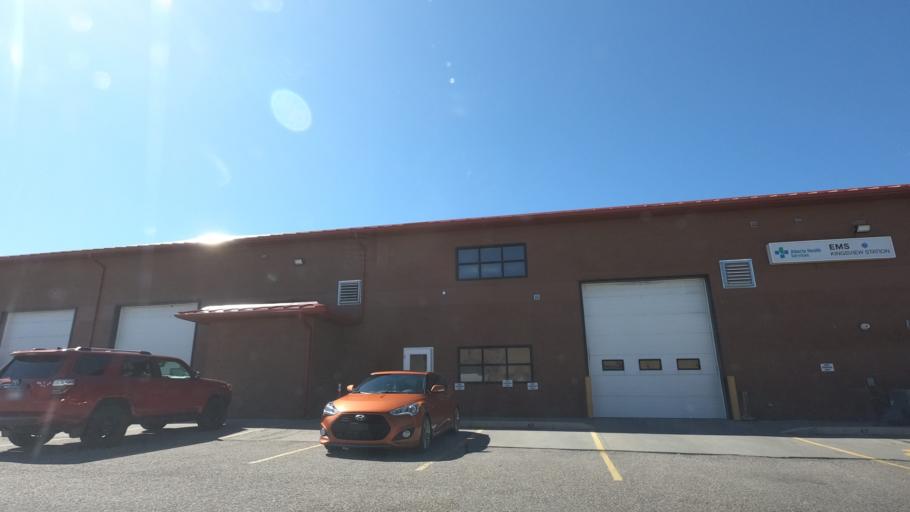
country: CA
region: Alberta
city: Airdrie
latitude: 51.2610
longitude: -113.9975
